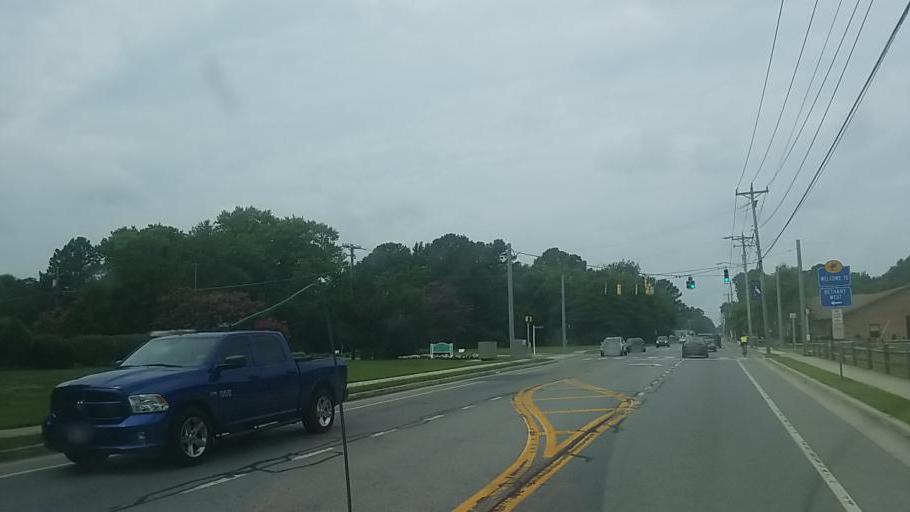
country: US
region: Delaware
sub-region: Sussex County
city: Bethany Beach
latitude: 38.5395
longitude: -75.0671
